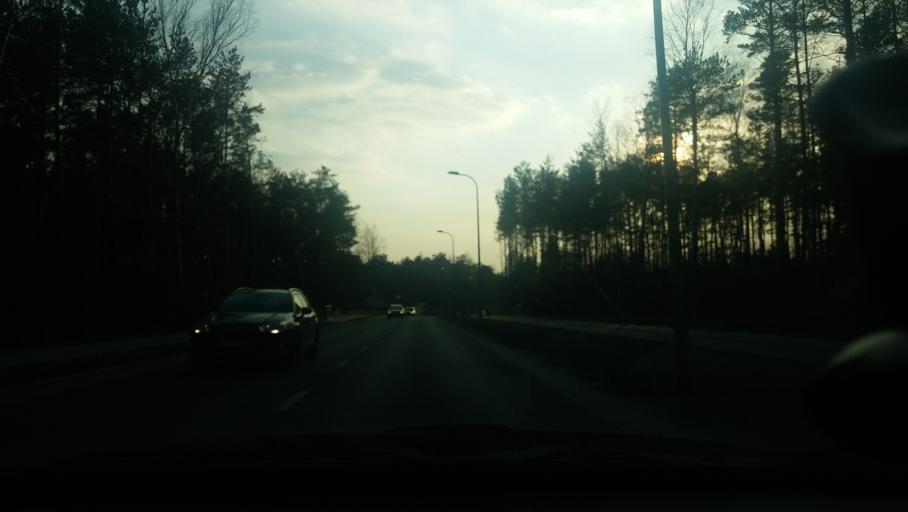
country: PL
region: Masovian Voivodeship
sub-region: Warszawa
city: Wawer
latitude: 52.2122
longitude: 21.2141
